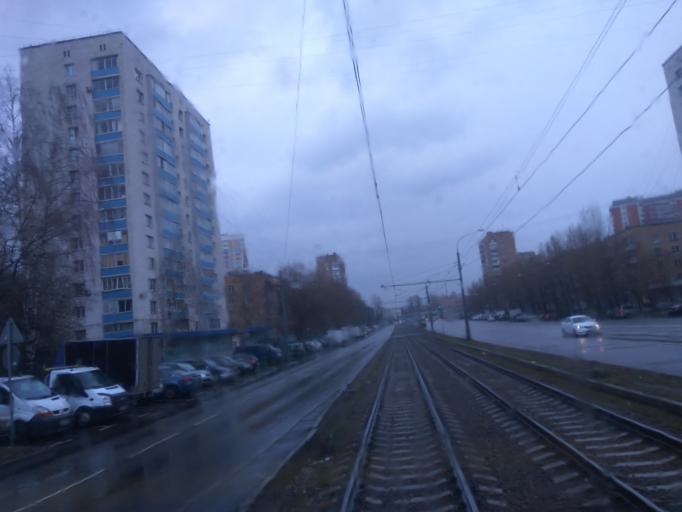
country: RU
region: Moscow
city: Kozeyevo
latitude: 55.8748
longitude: 37.6369
